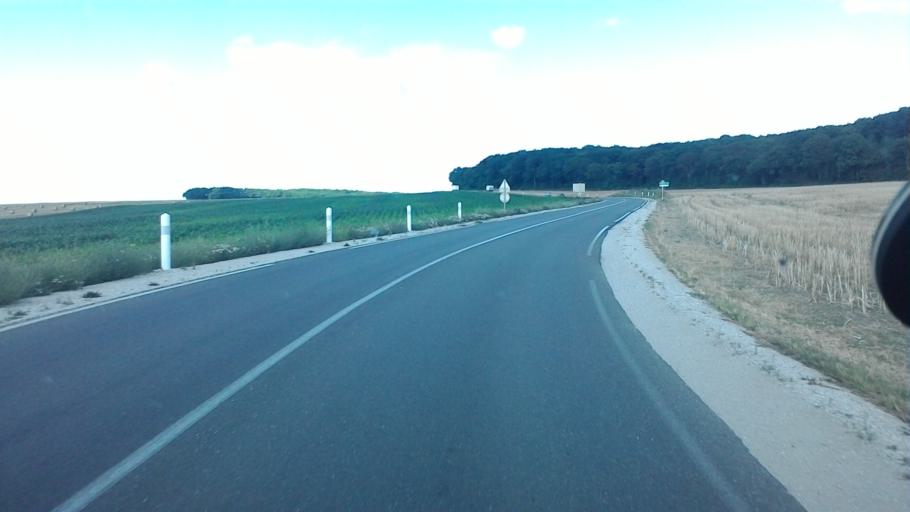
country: FR
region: Franche-Comte
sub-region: Departement de la Haute-Saone
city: Marnay
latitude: 47.3426
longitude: 5.7026
